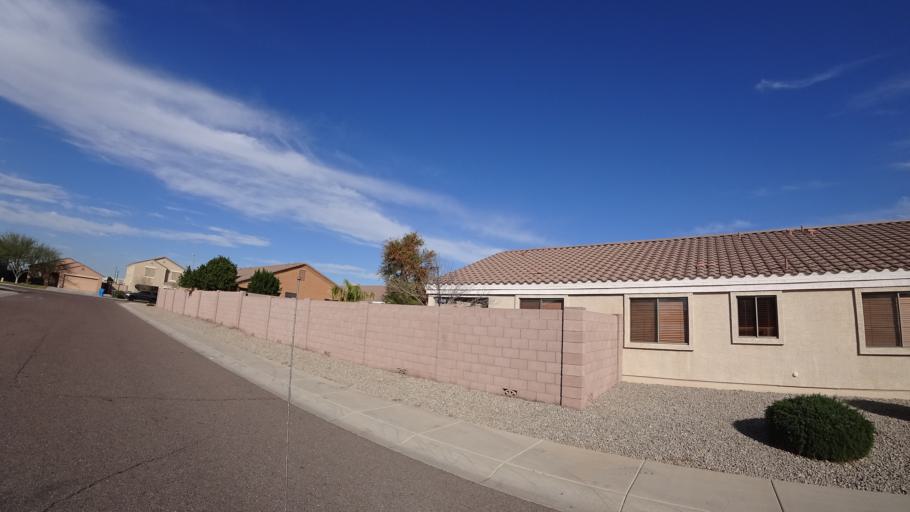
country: US
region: Arizona
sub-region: Maricopa County
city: Tolleson
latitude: 33.4322
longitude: -112.2890
